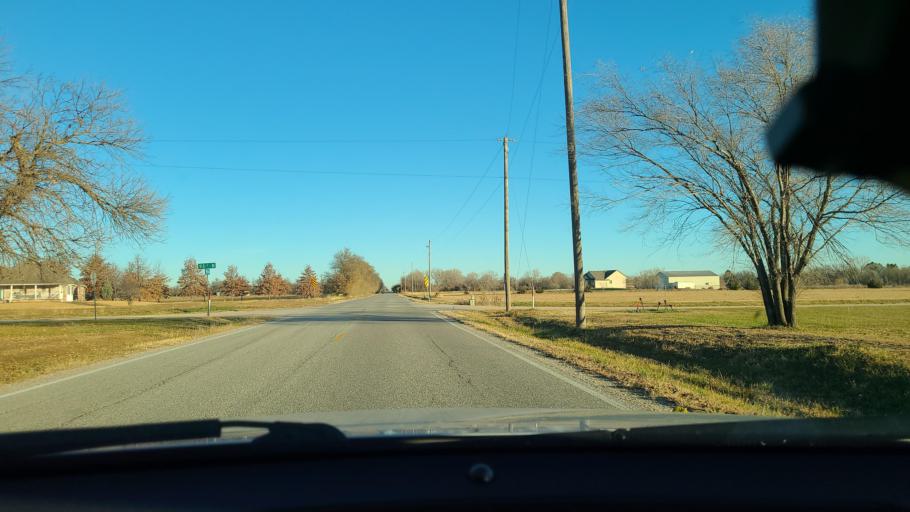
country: US
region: Kansas
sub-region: Sedgwick County
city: Park City
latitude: 37.8533
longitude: -97.3175
